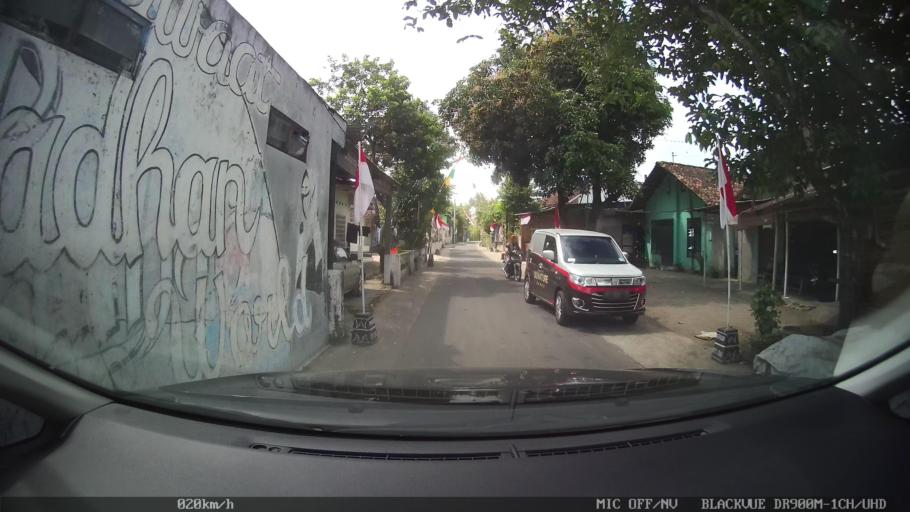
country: ID
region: Daerah Istimewa Yogyakarta
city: Kasihan
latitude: -7.8184
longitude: 110.3384
